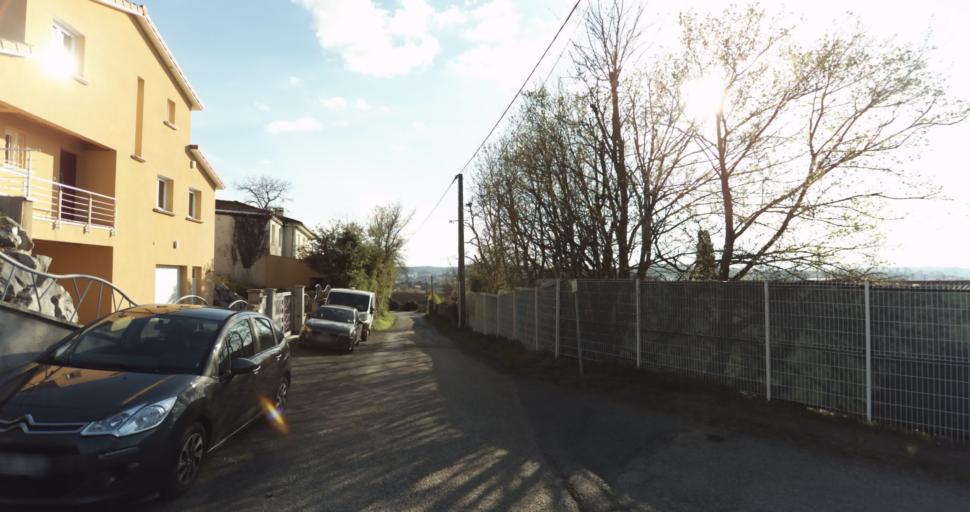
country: FR
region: Rhone-Alpes
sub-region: Departement de la Loire
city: La Talaudiere
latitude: 45.4586
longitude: 4.4269
